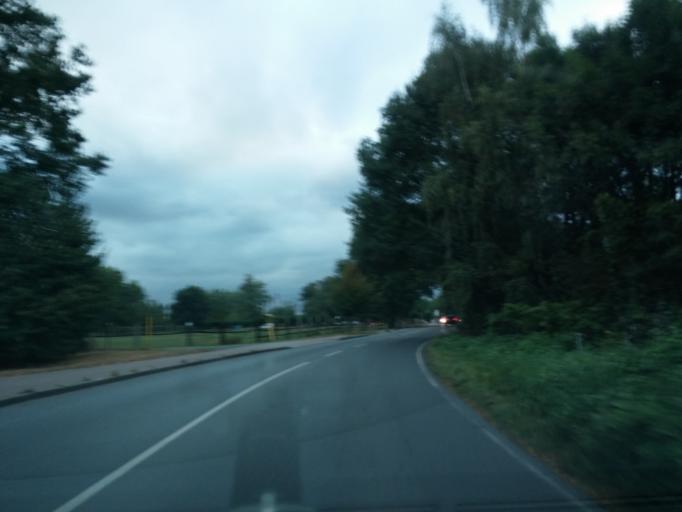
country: DE
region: North Rhine-Westphalia
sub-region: Regierungsbezirk Munster
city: Gladbeck
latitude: 51.5669
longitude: 7.0278
